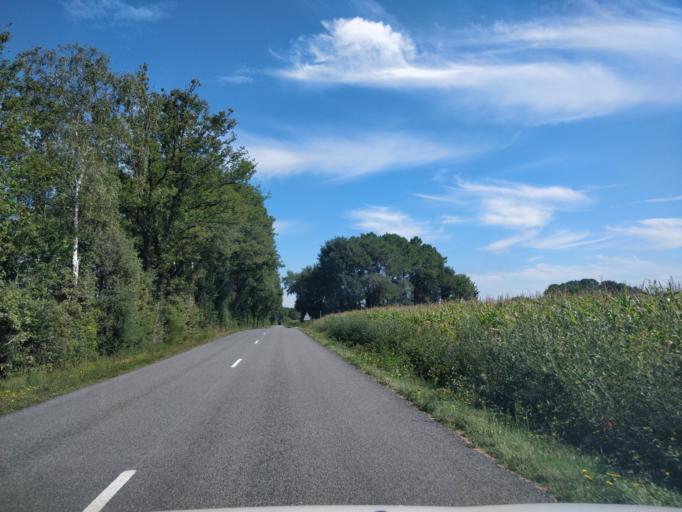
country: FR
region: Pays de la Loire
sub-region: Departement de la Loire-Atlantique
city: Conquereuil
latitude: 47.6689
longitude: -1.7754
